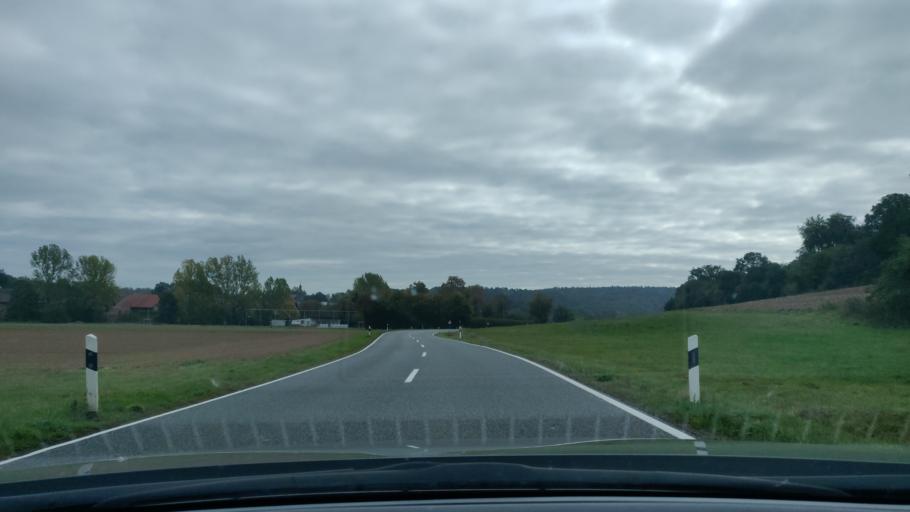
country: DE
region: Hesse
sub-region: Regierungsbezirk Kassel
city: Neuental
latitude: 50.9983
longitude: 9.2050
